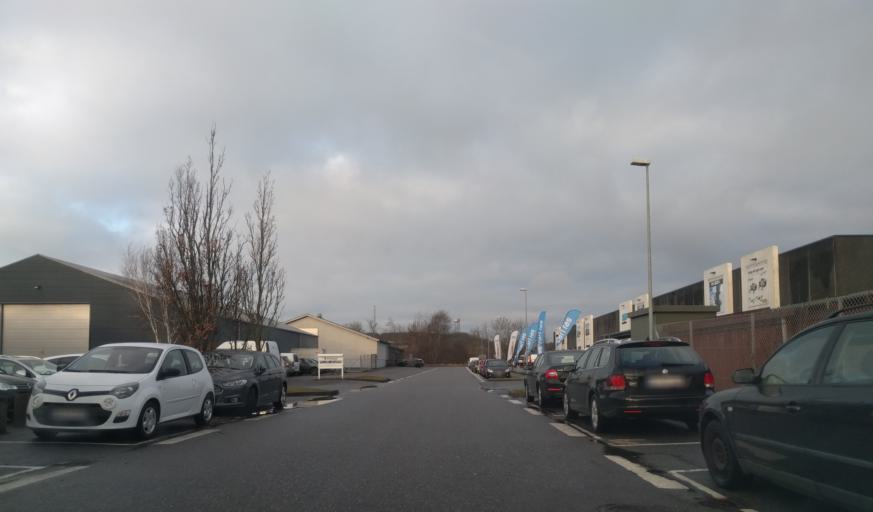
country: DK
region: North Denmark
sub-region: Alborg Kommune
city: Aalborg
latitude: 57.0375
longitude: 9.9257
